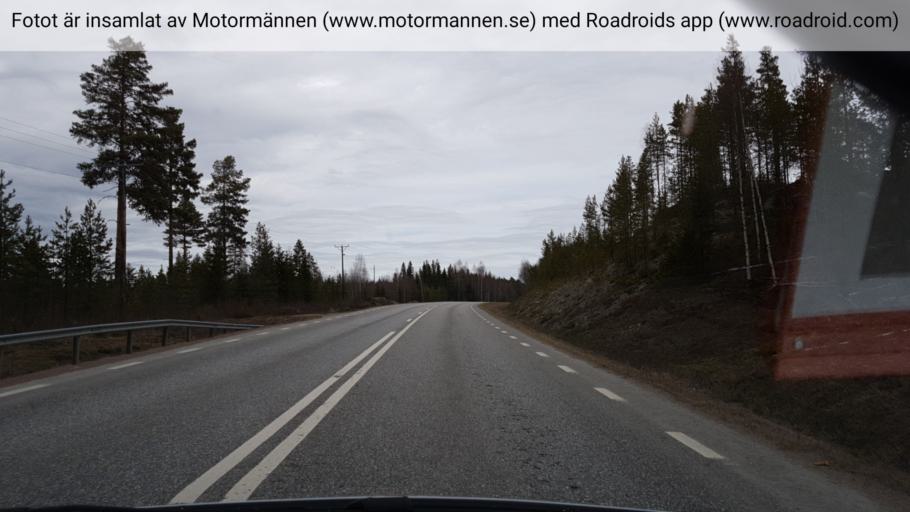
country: SE
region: Vaesternorrland
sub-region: Solleftea Kommun
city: As
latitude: 63.6724
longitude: 16.7955
